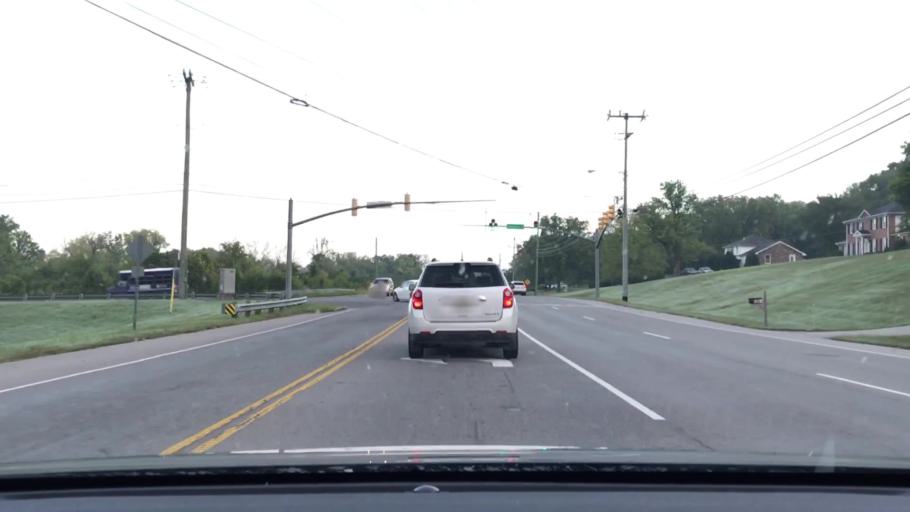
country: US
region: Tennessee
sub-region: Williamson County
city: Brentwood Estates
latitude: 36.0299
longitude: -86.7441
